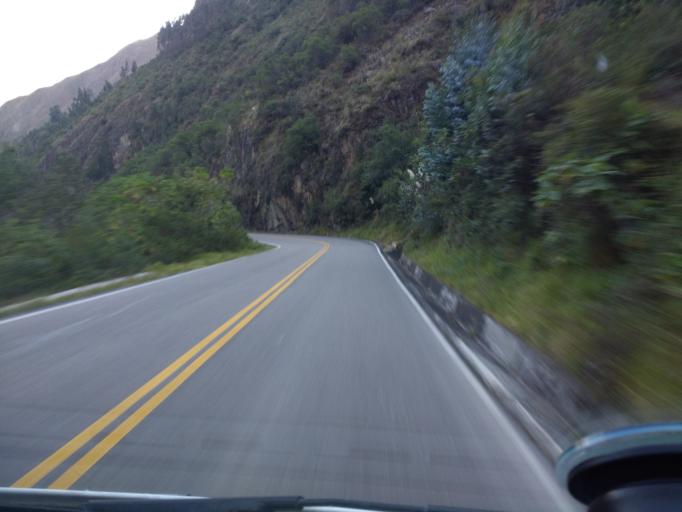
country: PE
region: Cusco
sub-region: Provincia de Urubamba
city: Ollantaytambo
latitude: -13.1996
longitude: -72.2953
